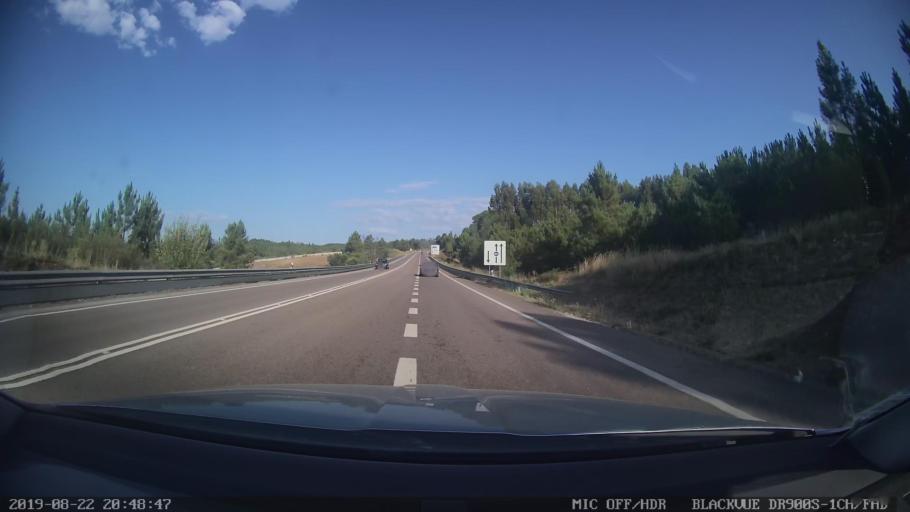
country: PT
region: Castelo Branco
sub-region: Proenca-A-Nova
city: Proenca-a-Nova
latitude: 39.7363
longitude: -7.9176
